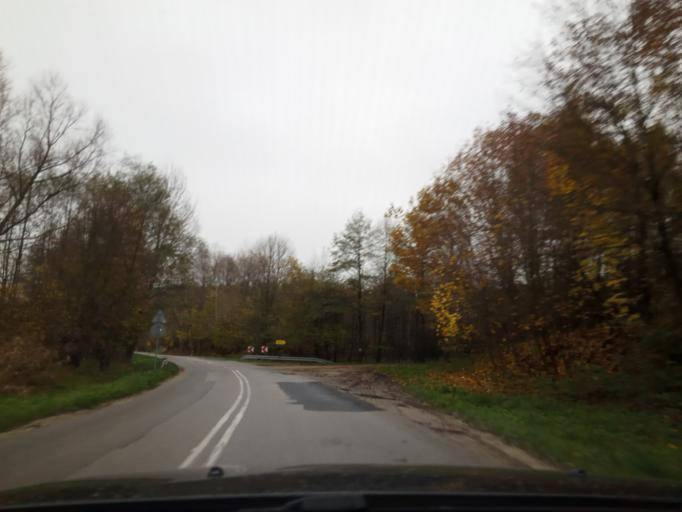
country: PL
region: Swietokrzyskie
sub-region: Powiat pinczowski
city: Dzialoszyce
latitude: 50.4140
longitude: 20.3242
